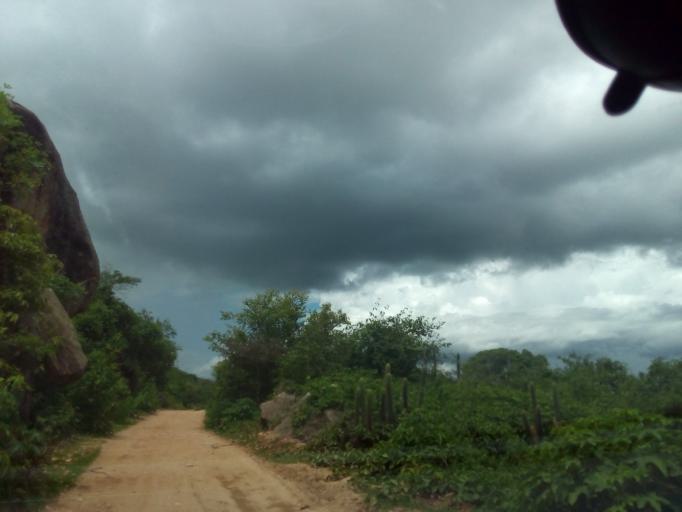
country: BR
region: Rio Grande do Norte
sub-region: Sao Tome
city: Sao Tome
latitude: -5.9521
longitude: -35.9213
